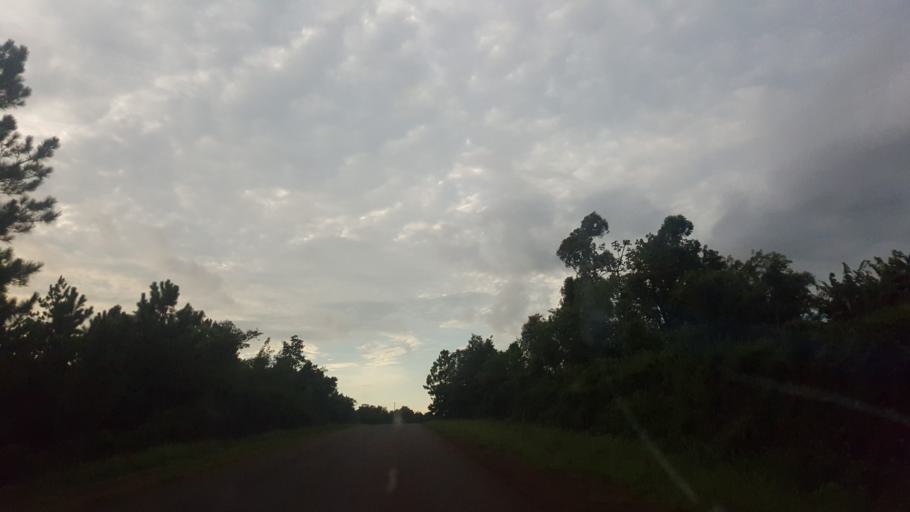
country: AR
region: Misiones
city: Dos de Mayo
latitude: -26.9418
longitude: -54.7157
